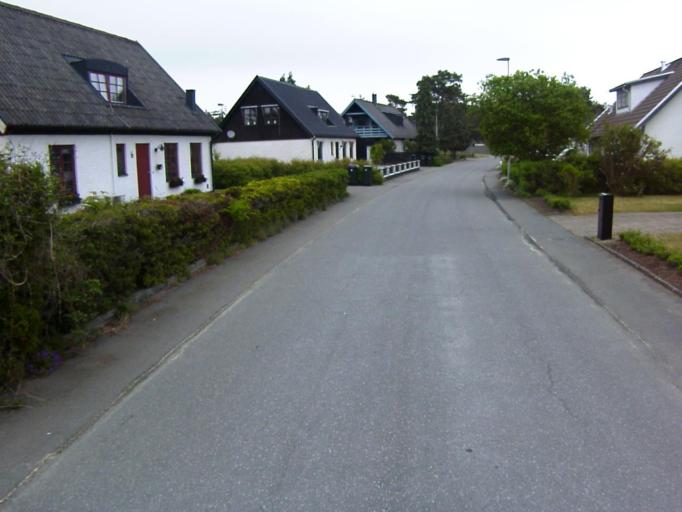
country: SE
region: Skane
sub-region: Kristianstads Kommun
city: Ahus
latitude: 55.9391
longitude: 14.2818
